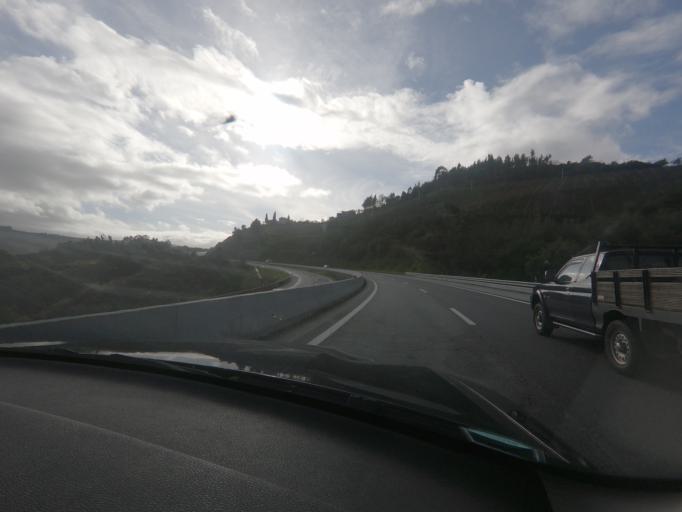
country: PT
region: Viseu
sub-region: Lamego
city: Lamego
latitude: 41.0966
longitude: -7.7824
